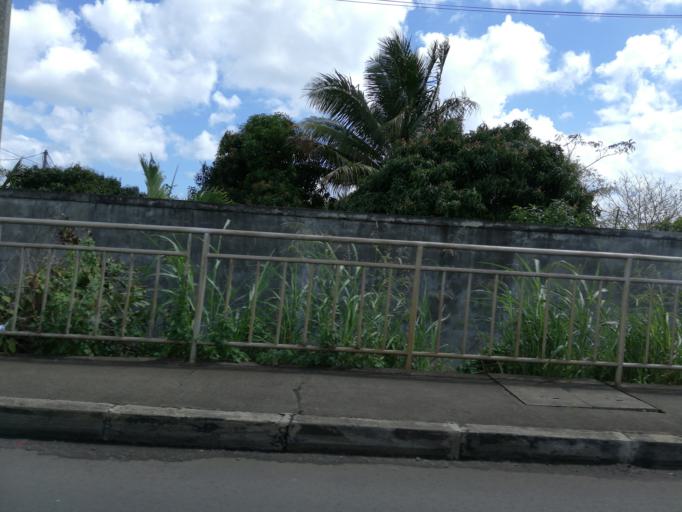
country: MU
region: Pamplemousses
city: Triolet
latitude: -20.0428
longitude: 57.5573
